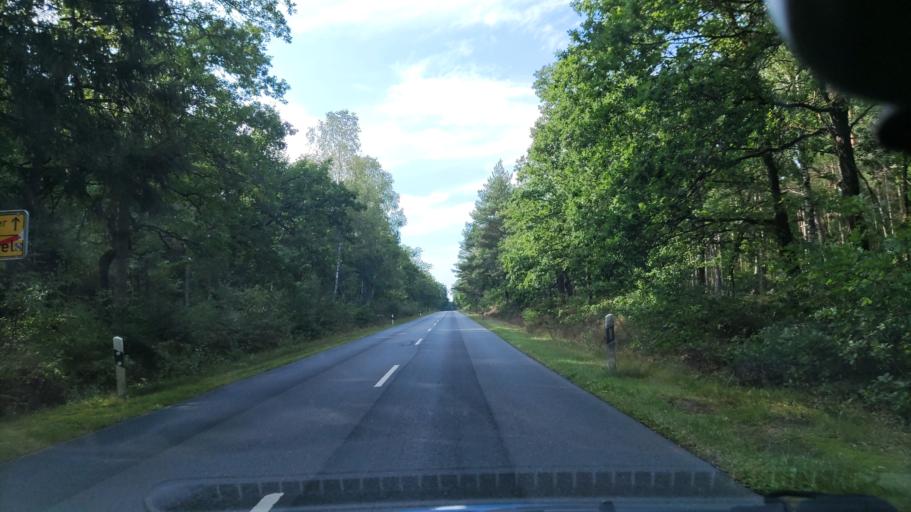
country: DE
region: Lower Saxony
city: Fassberg
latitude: 52.9652
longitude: 10.1728
